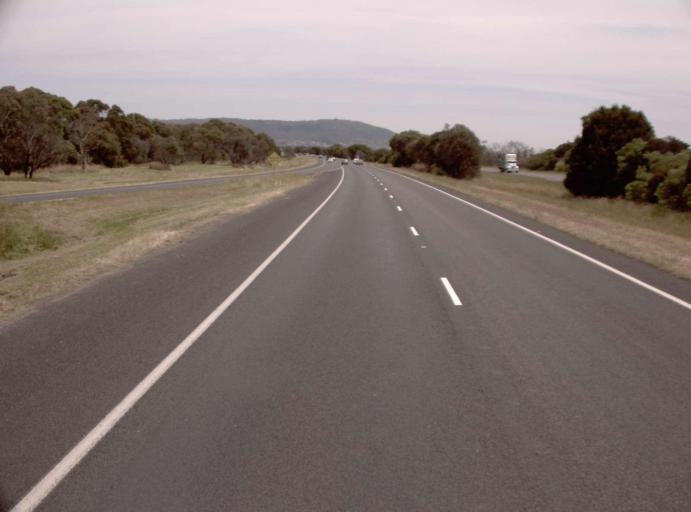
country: AU
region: Victoria
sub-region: Mornington Peninsula
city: Safety Beach
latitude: -38.3045
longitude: 145.0261
